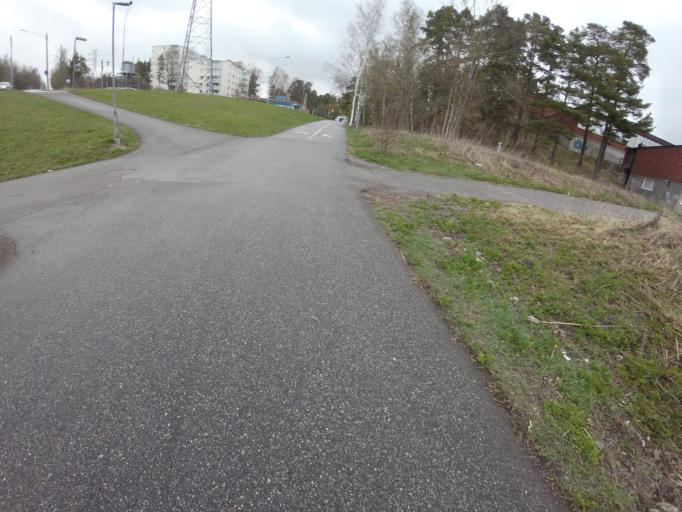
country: FI
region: Varsinais-Suomi
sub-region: Turku
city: Raisio
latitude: 60.4537
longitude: 22.1571
